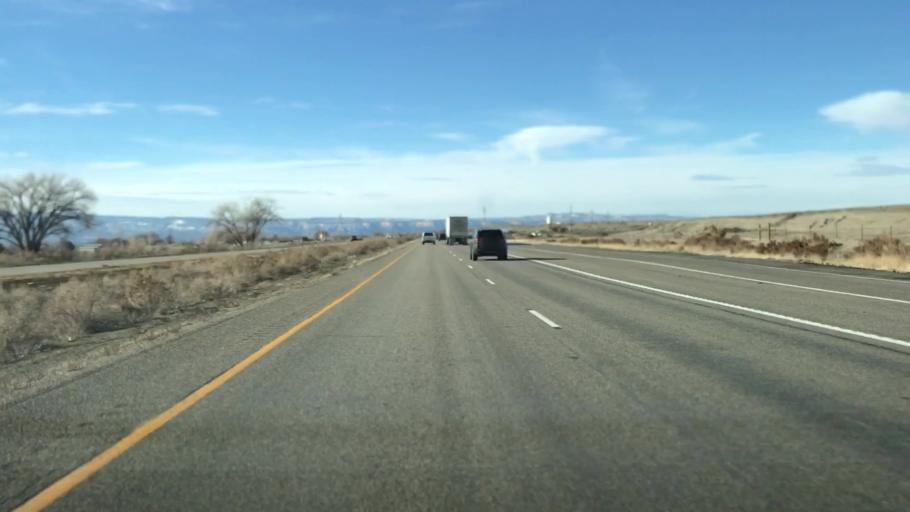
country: US
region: Colorado
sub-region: Mesa County
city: Clifton
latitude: 39.1105
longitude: -108.4187
